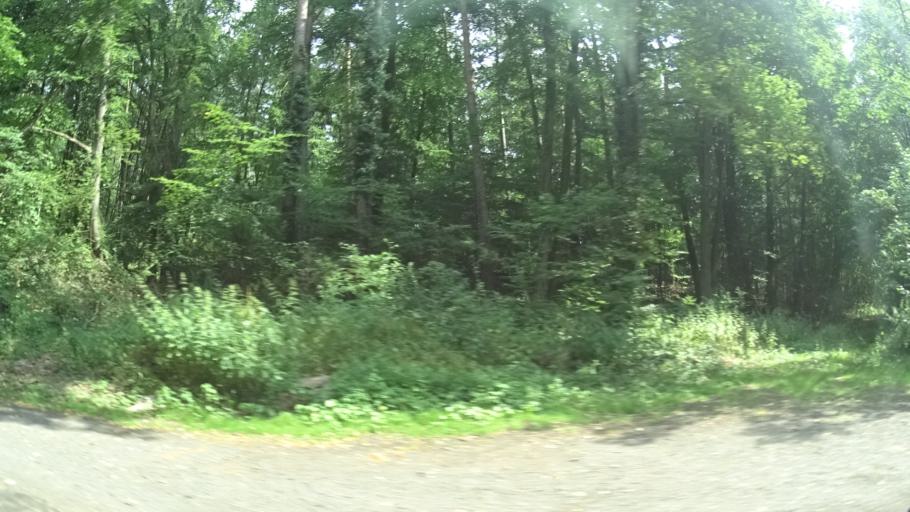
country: DE
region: Hesse
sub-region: Regierungsbezirk Giessen
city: Lauterbach
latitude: 50.6068
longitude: 9.4319
